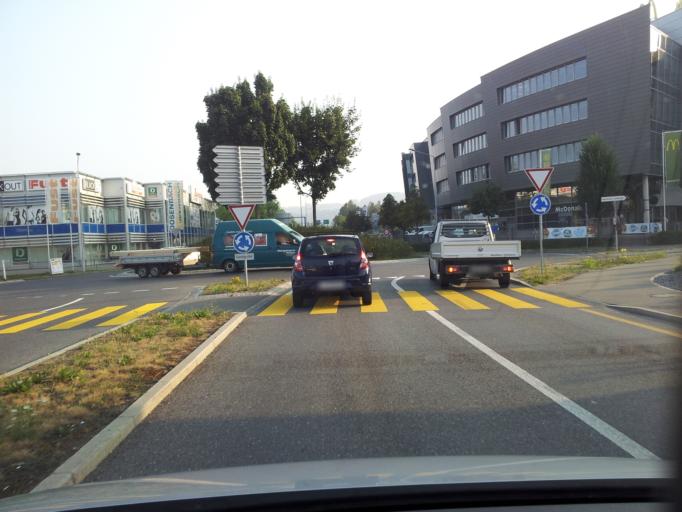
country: CH
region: Lucerne
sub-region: Sursee District
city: Sursee
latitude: 47.1772
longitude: 8.1097
